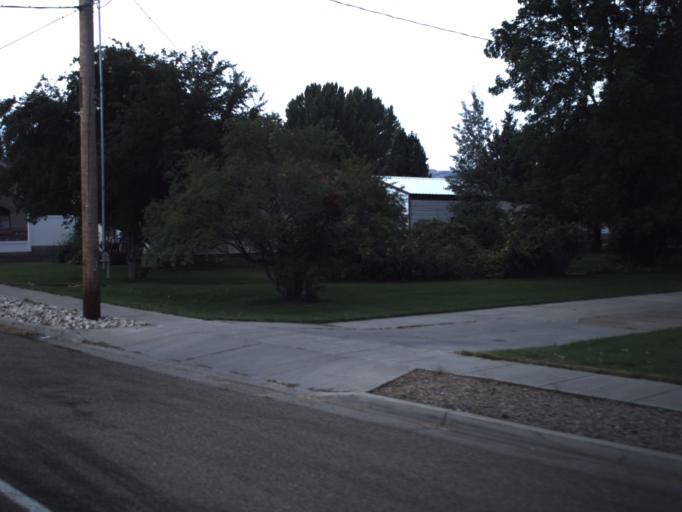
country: US
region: Utah
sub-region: Morgan County
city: Morgan
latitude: 41.0405
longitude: -111.6797
